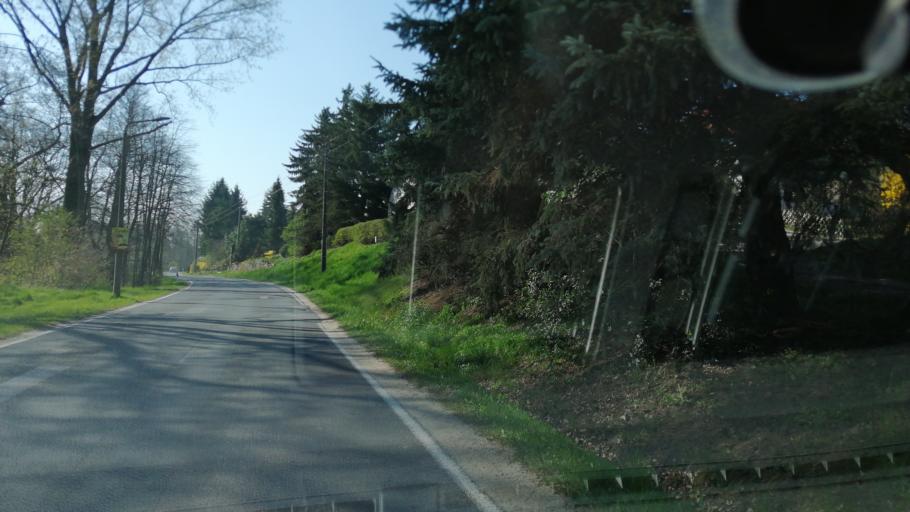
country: DE
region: Saxony
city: Goerlitz
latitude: 51.1703
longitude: 14.9355
